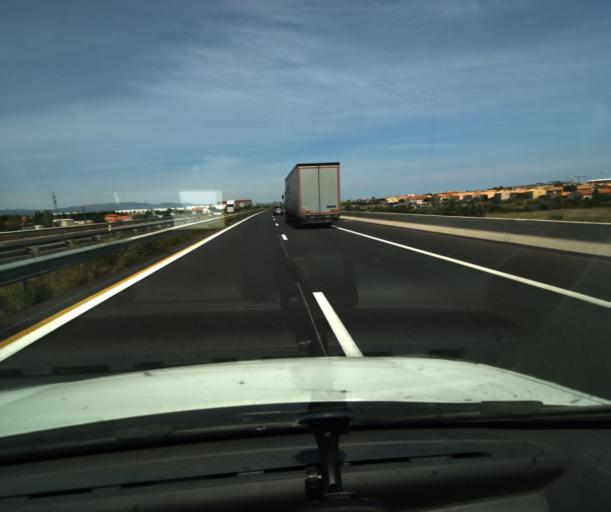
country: FR
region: Languedoc-Roussillon
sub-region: Departement des Pyrenees-Orientales
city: Saint-Esteve
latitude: 42.7191
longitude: 2.8735
